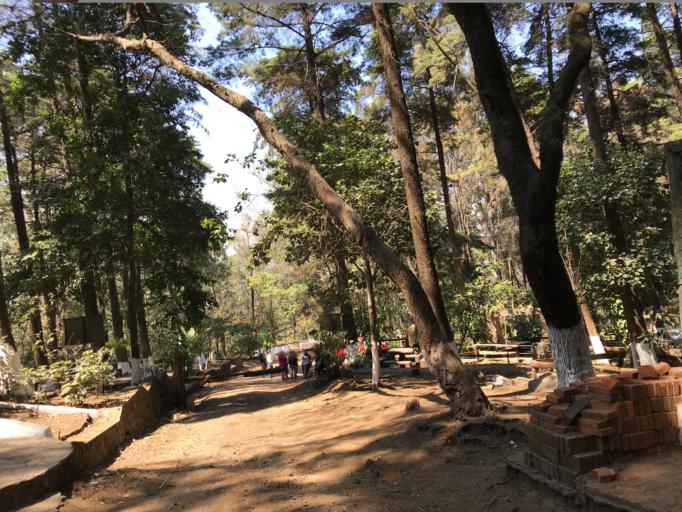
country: GT
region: Guatemala
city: Petapa
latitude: 14.4832
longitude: -90.5567
